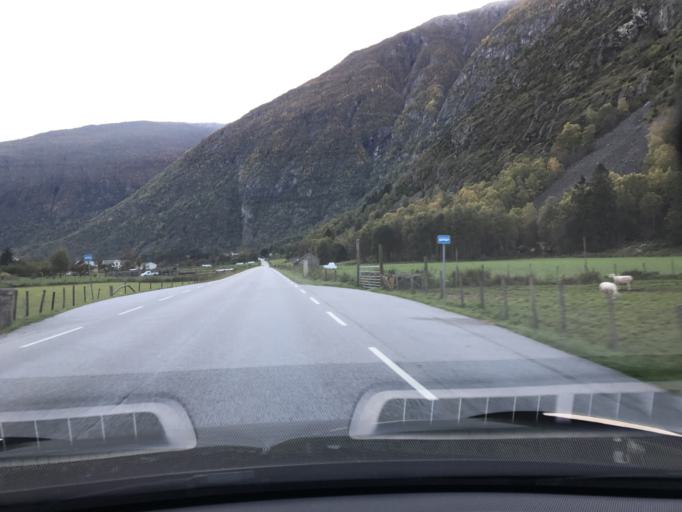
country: NO
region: Sogn og Fjordane
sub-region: Laerdal
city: Laerdalsoyri
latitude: 61.0834
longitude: 7.5086
